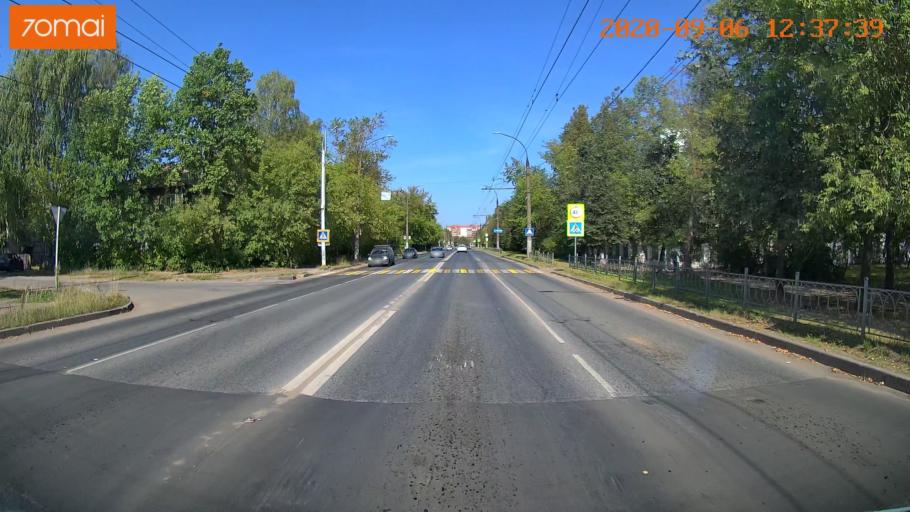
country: RU
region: Ivanovo
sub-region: Gorod Ivanovo
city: Ivanovo
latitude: 57.0284
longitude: 40.9802
